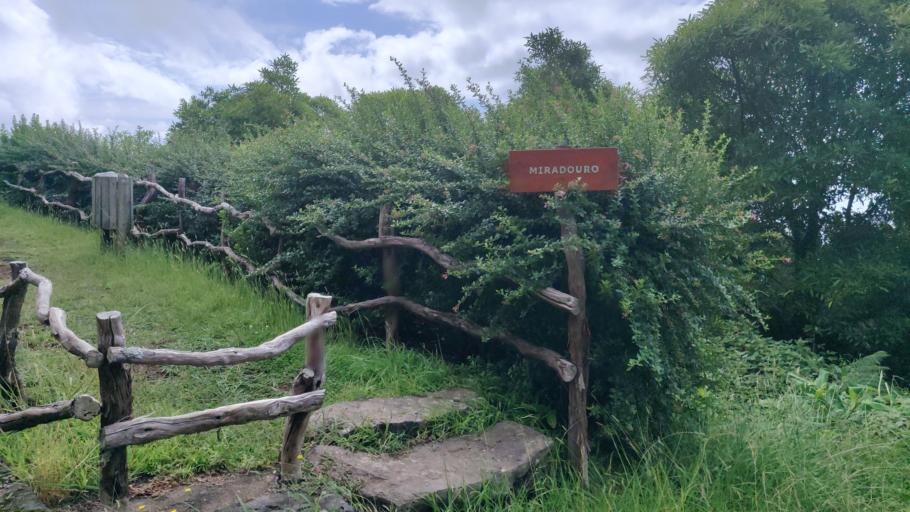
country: PT
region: Azores
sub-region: Sao Roque do Pico
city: Sao Roque do Pico
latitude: 38.5925
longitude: -27.9485
